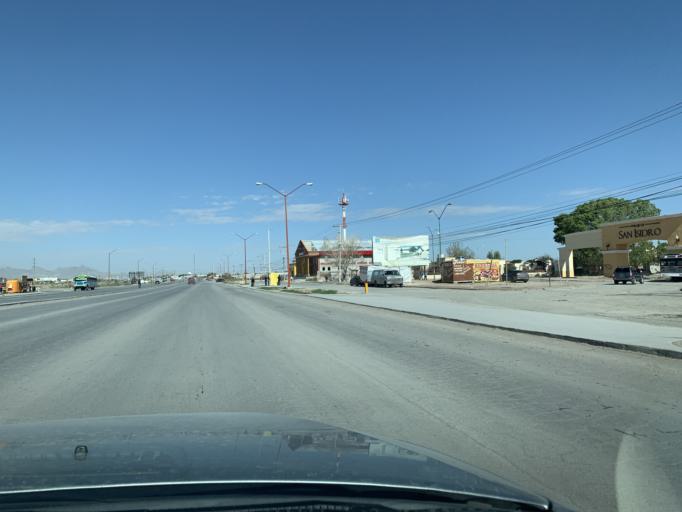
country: US
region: Texas
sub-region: El Paso County
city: San Elizario
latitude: 31.5809
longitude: -106.3600
